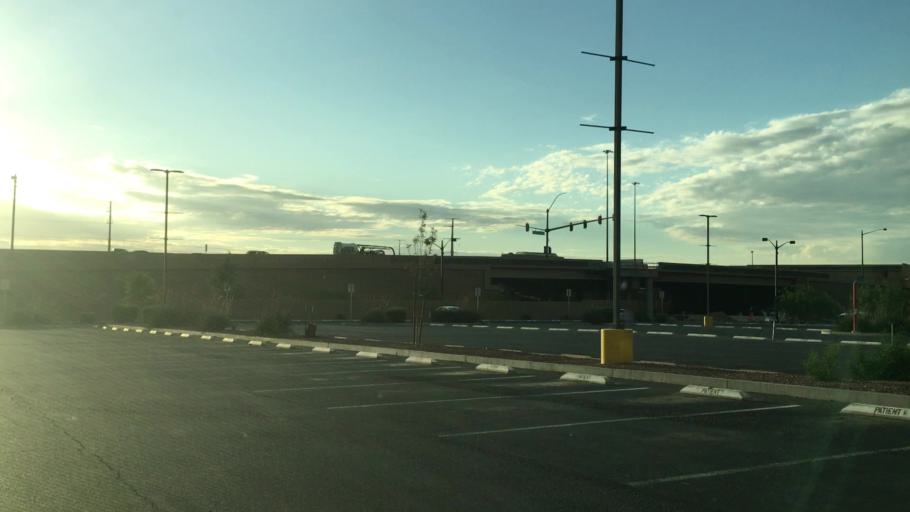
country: US
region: Nevada
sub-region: Clark County
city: Las Vegas
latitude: 36.1599
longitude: -115.1629
